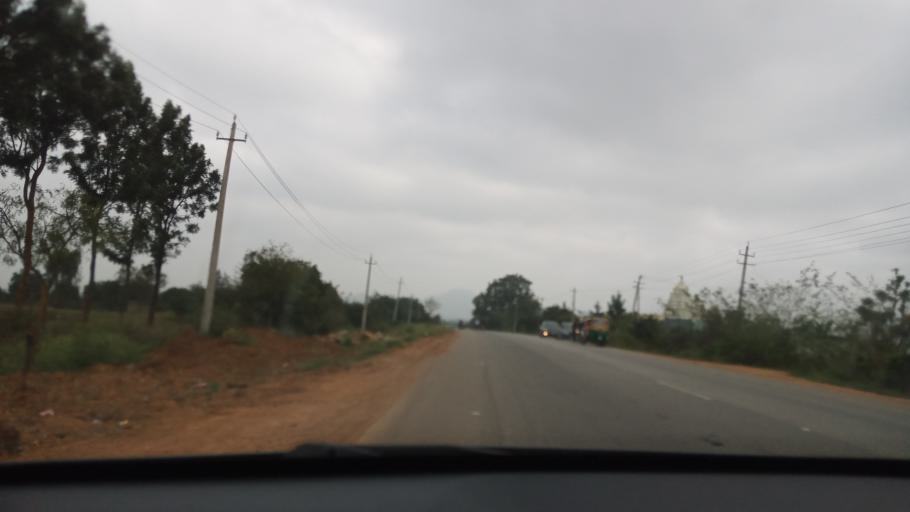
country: IN
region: Karnataka
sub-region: Chikkaballapur
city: Sidlaghatta
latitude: 13.2899
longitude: 77.9634
